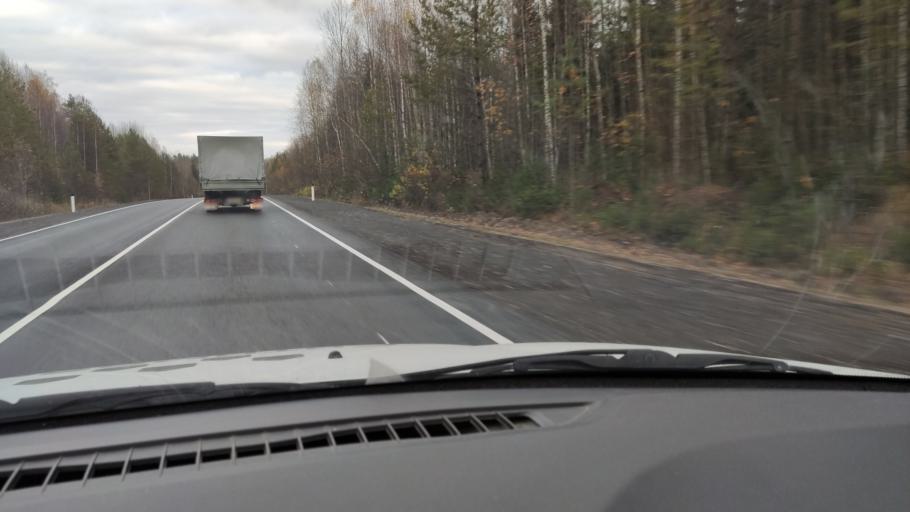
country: RU
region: Kirov
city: Chernaya Kholunitsa
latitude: 58.8729
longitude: 51.5160
